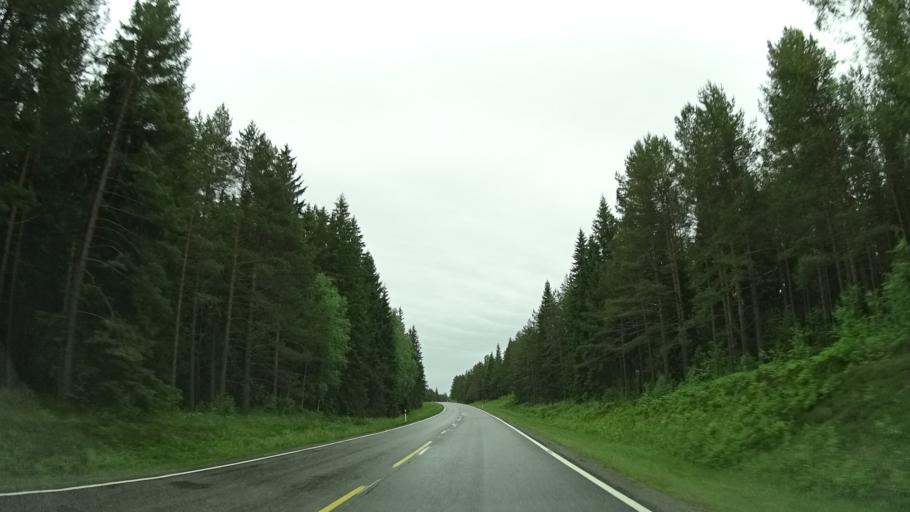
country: FI
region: Varsinais-Suomi
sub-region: Salo
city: Pernioe
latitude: 60.1064
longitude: 23.2153
